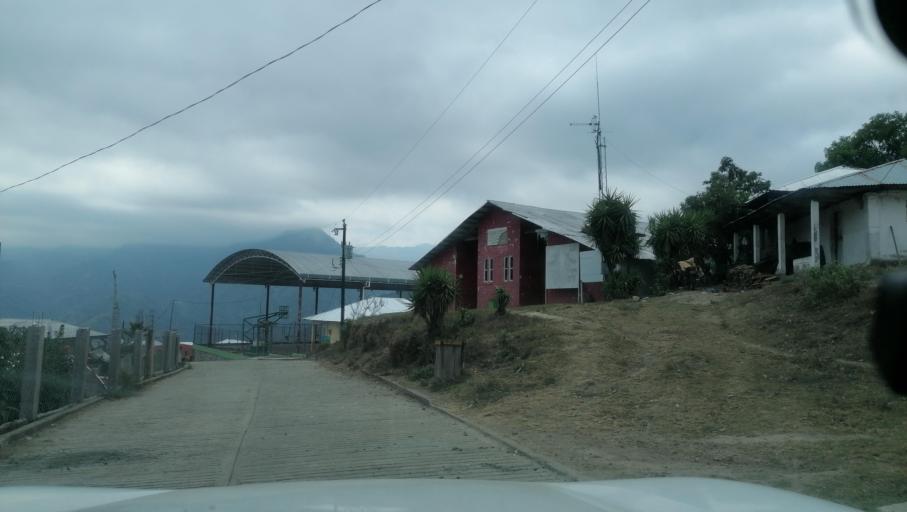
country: GT
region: San Marcos
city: Sibinal
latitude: 15.1643
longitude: -92.1546
